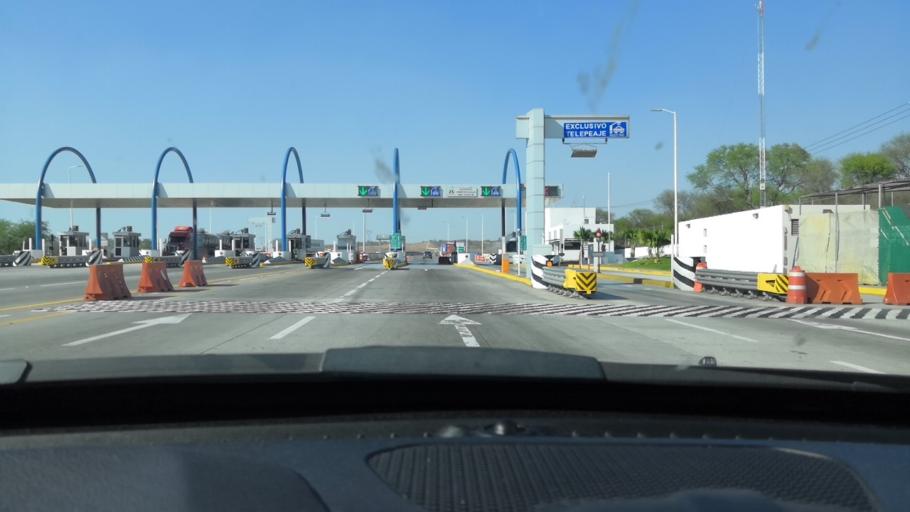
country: MX
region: Jalisco
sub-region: Zapotlanejo
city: La Mezquitera
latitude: 20.5721
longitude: -103.1013
